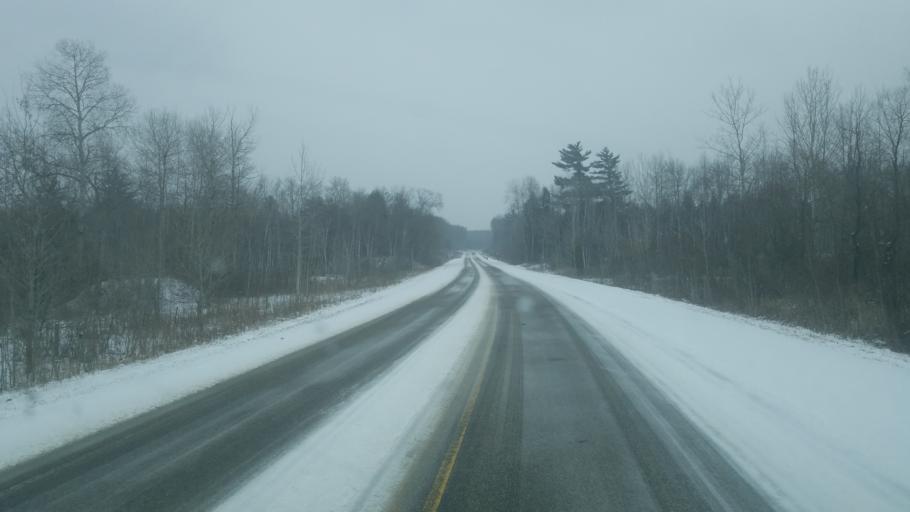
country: US
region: Michigan
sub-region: Osceola County
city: Evart
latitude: 43.8751
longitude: -85.3601
